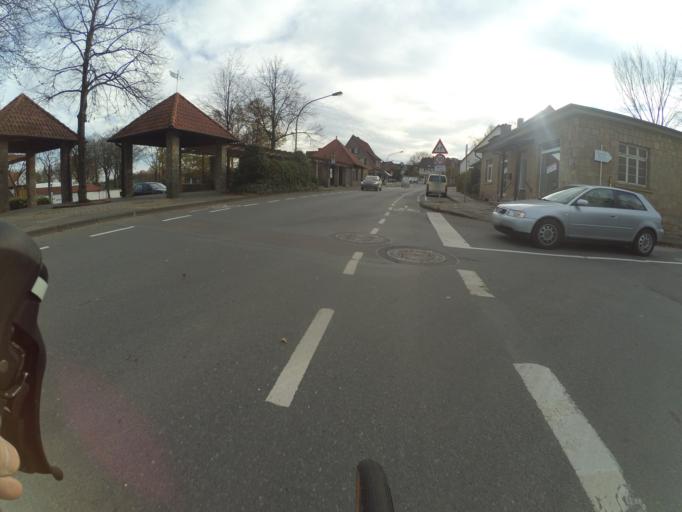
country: DE
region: North Rhine-Westphalia
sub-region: Regierungsbezirk Munster
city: Tecklenburg
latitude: 52.2611
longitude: 7.7900
